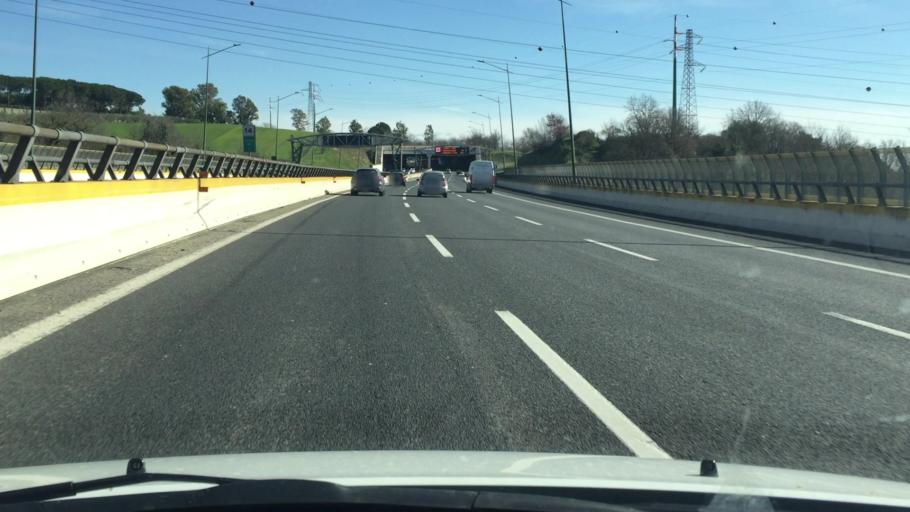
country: VA
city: Vatican City
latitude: 41.9821
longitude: 12.4458
